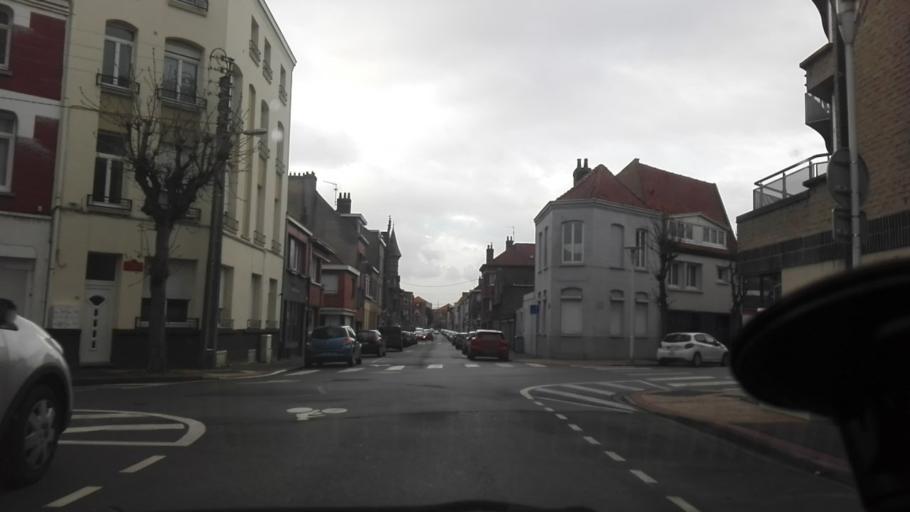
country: FR
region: Nord-Pas-de-Calais
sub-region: Departement du Nord
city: Coudekerque-Branche
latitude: 51.0452
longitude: 2.3979
